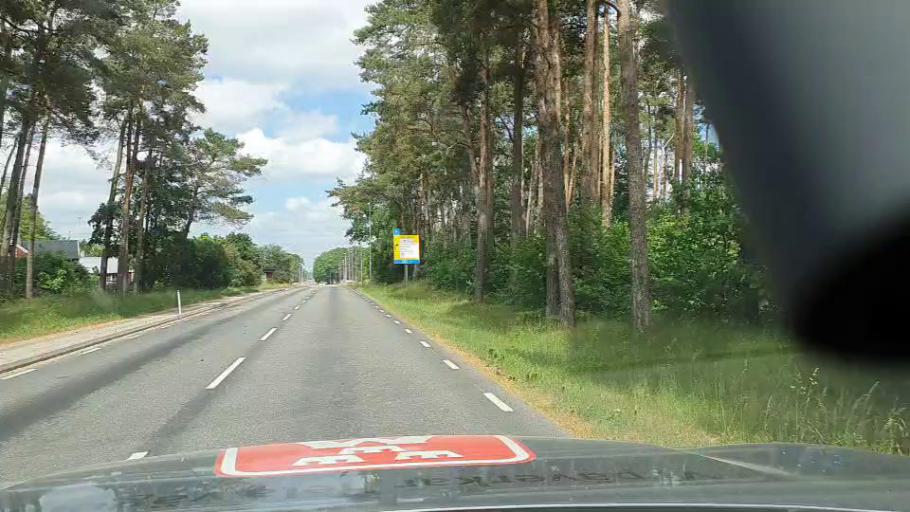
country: SE
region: Blekinge
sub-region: Karlshamns Kommun
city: Morrum
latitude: 56.1142
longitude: 14.6754
